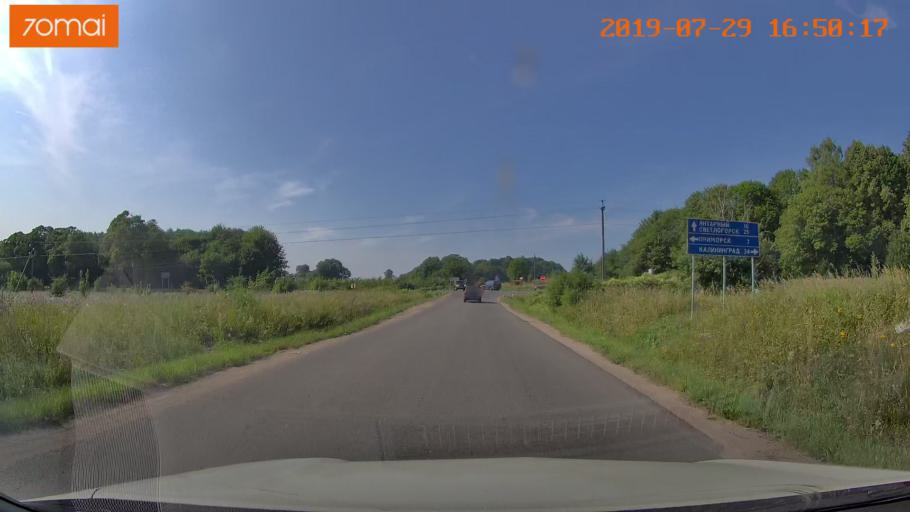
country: RU
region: Kaliningrad
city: Primorsk
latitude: 54.8019
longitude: 20.0566
